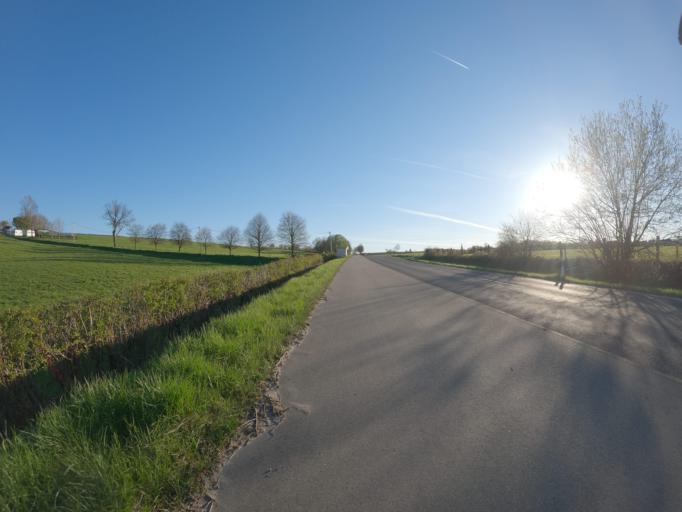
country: DE
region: North Rhine-Westphalia
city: Stolberg
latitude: 50.7780
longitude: 6.2600
